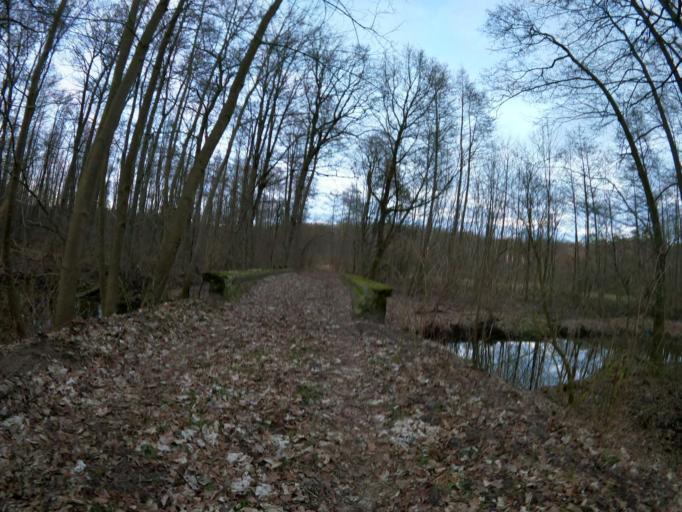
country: PL
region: West Pomeranian Voivodeship
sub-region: Powiat kamienski
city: Golczewo
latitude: 53.8330
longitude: 14.9556
